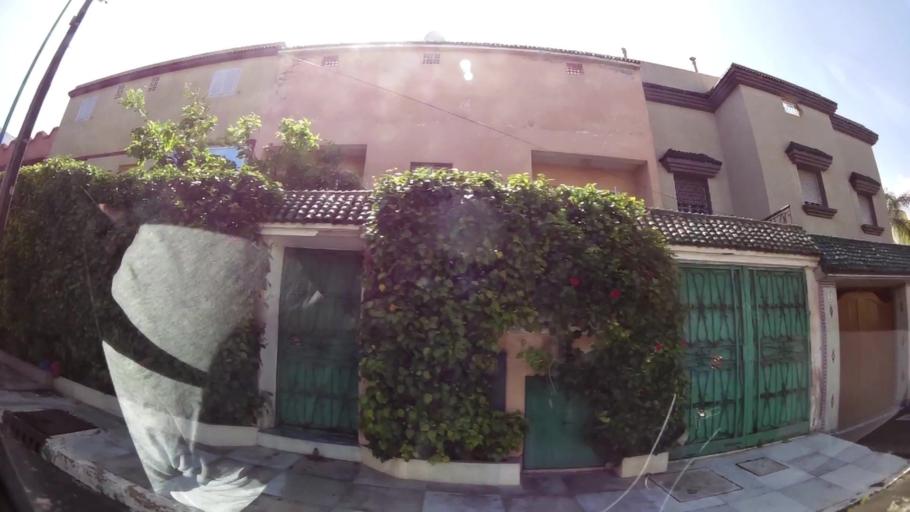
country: MA
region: Grand Casablanca
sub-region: Mediouna
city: Tit Mellil
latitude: 33.6168
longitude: -7.5224
